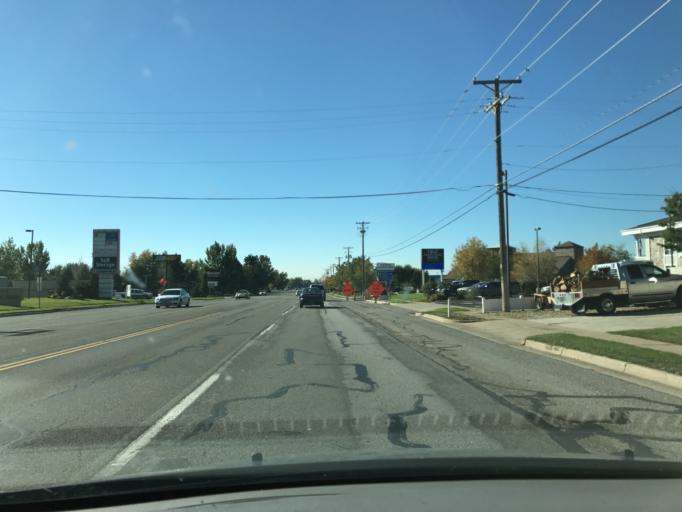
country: US
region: Utah
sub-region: Davis County
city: Layton
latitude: 41.0835
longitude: -111.9735
